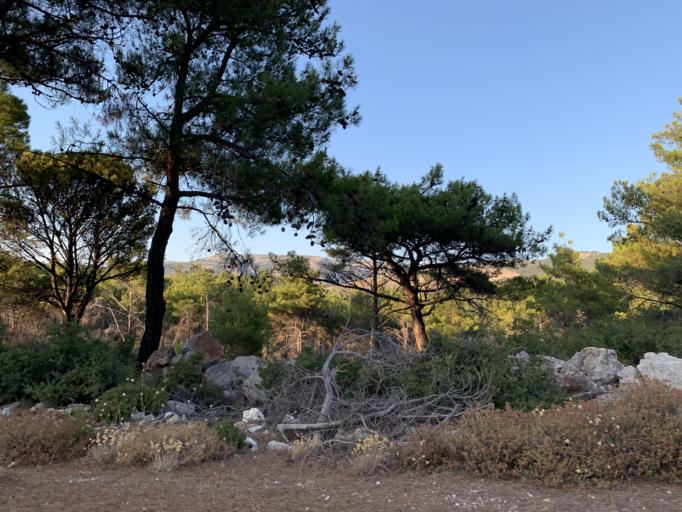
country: GR
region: North Aegean
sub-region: Chios
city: Vrontados
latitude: 38.3807
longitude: 26.0186
